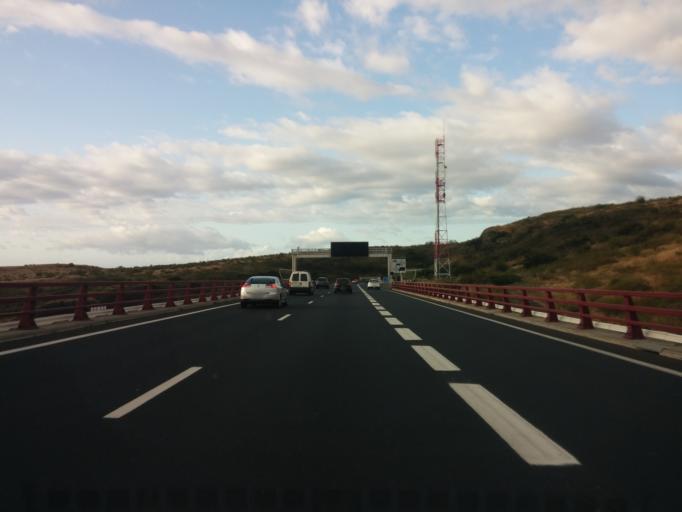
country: RE
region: Reunion
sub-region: Reunion
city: Saint-Paul
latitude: -21.0348
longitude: 55.2496
